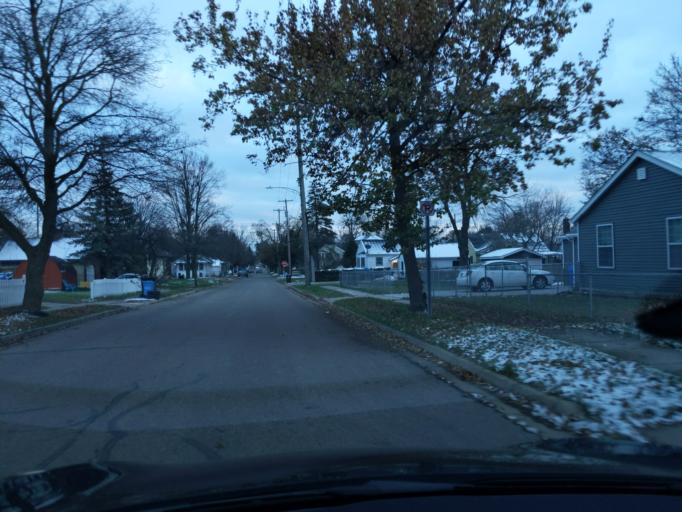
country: US
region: Michigan
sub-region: Ingham County
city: Lansing
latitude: 42.7612
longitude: -84.5407
